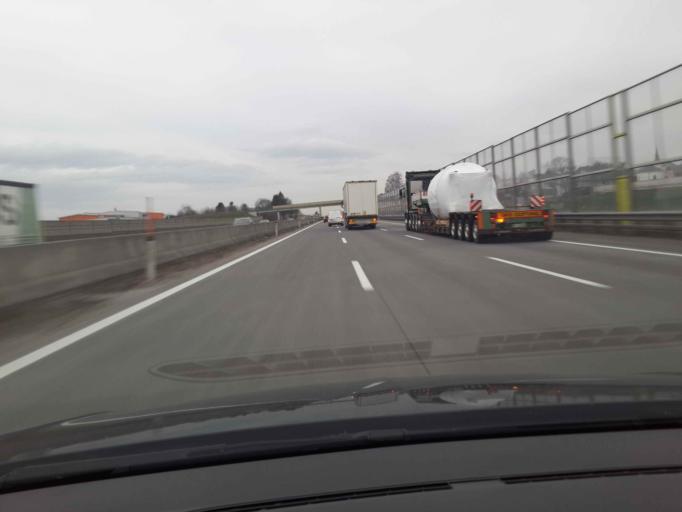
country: AT
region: Lower Austria
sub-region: Politischer Bezirk Amstetten
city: Amstetten
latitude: 48.1469
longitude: 14.8956
